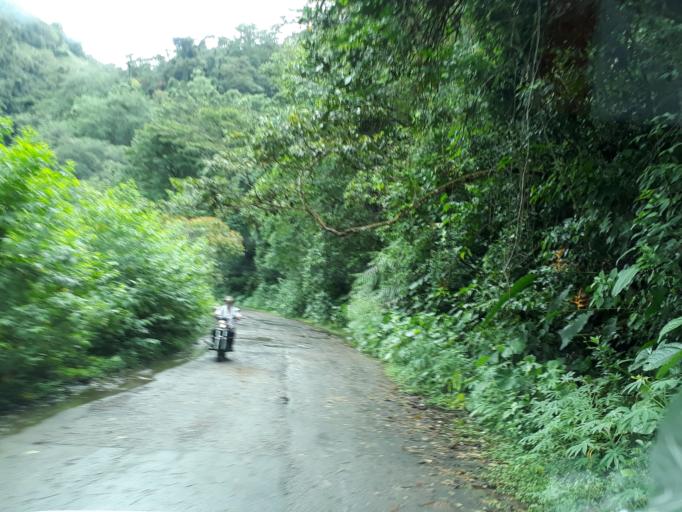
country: CO
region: Boyaca
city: Santa Maria
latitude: 4.7386
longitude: -73.3102
